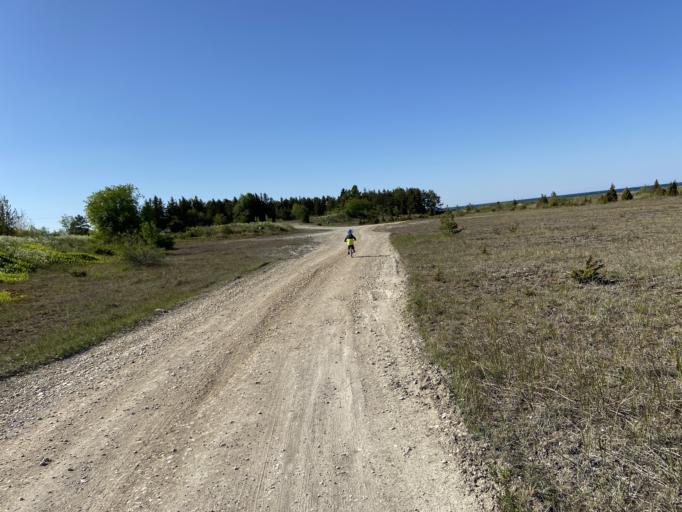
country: EE
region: Harju
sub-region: Paldiski linn
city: Paldiski
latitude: 59.2687
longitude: 23.7391
